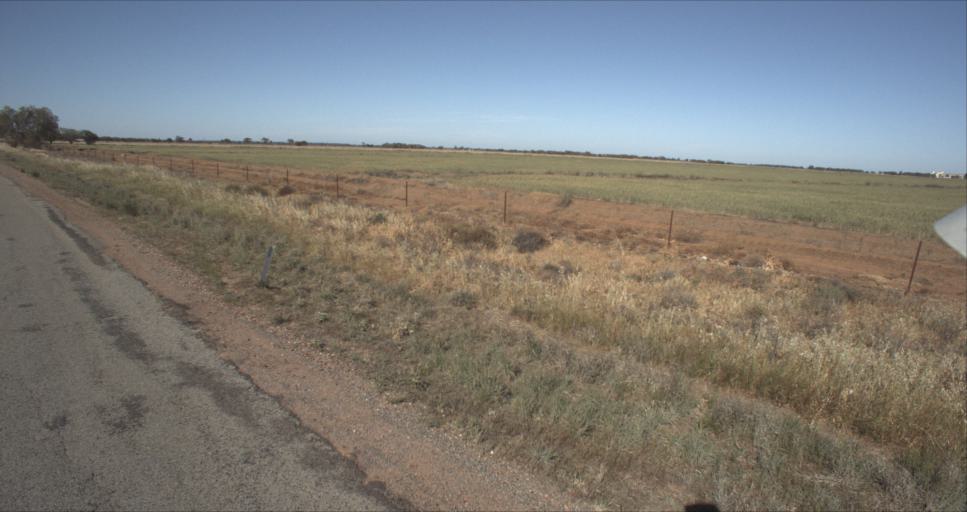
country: AU
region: New South Wales
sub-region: Leeton
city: Leeton
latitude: -34.5579
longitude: 146.3133
